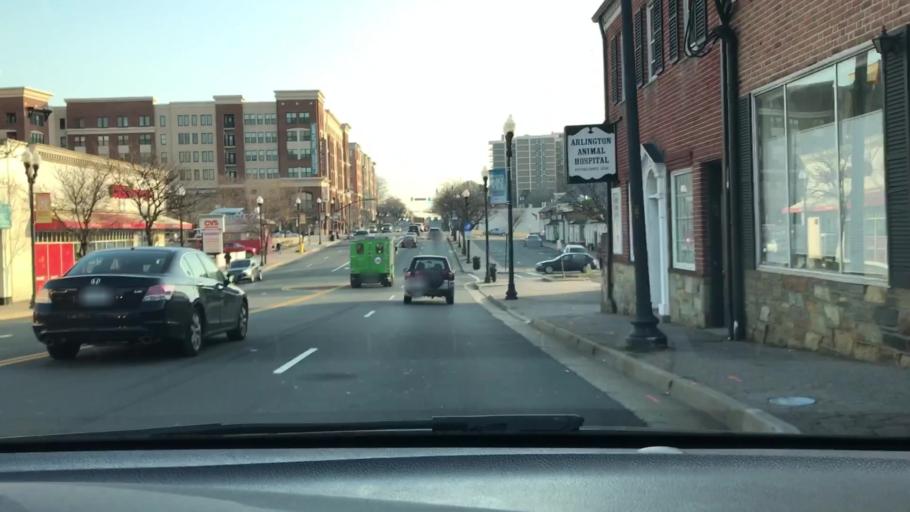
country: US
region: Virginia
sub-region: Arlington County
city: Arlington
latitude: 38.8629
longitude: -77.0857
